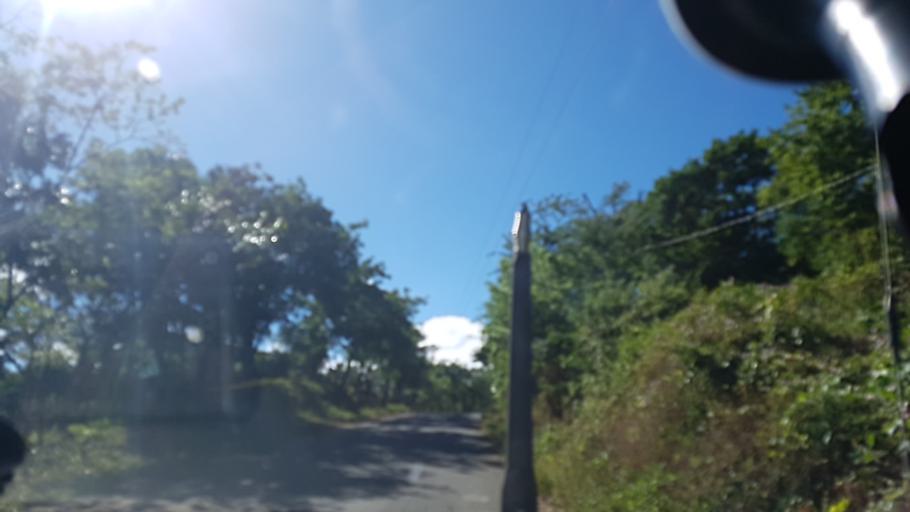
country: NI
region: Carazo
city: Santa Teresa
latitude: 11.6719
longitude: -86.1824
